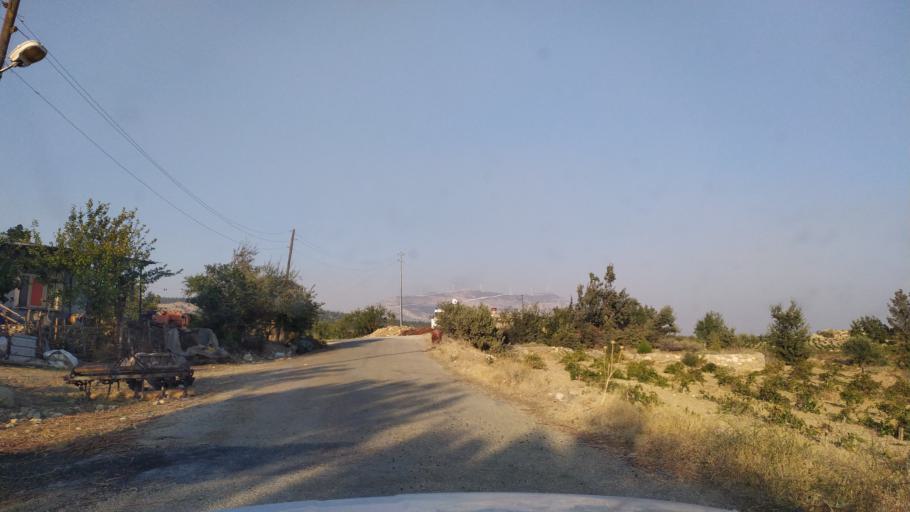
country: TR
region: Mersin
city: Mut
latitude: 36.6828
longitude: 33.1920
